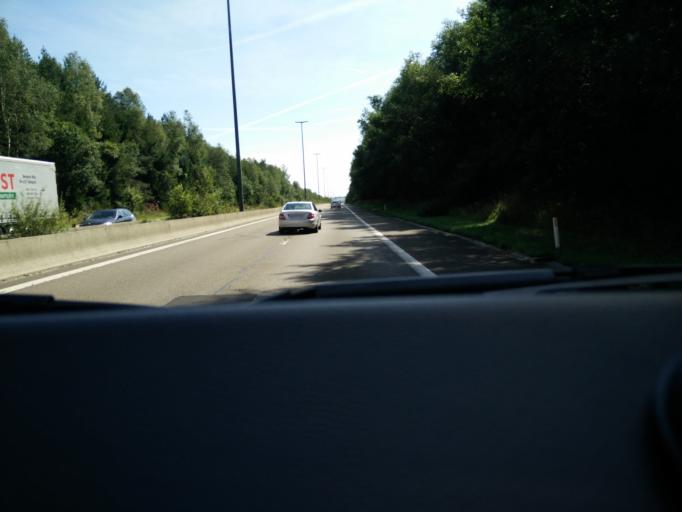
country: BE
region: Wallonia
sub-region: Province du Luxembourg
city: Neufchateau
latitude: 49.8833
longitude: 5.4268
